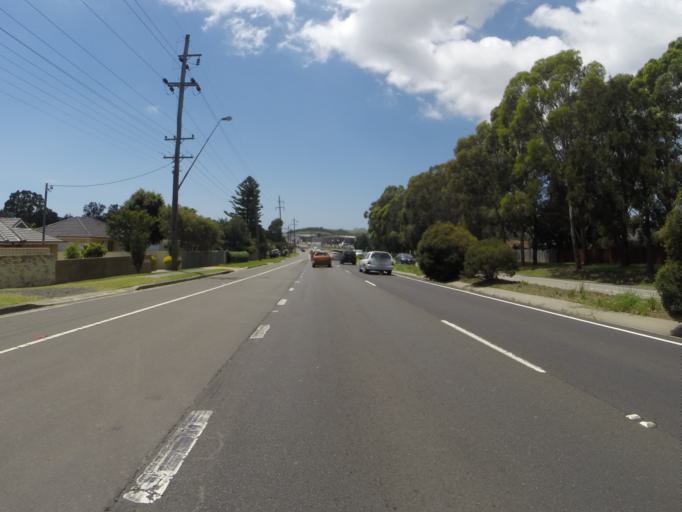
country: AU
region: New South Wales
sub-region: Shellharbour
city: Albion Park Rail
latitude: -34.5699
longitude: 150.8115
